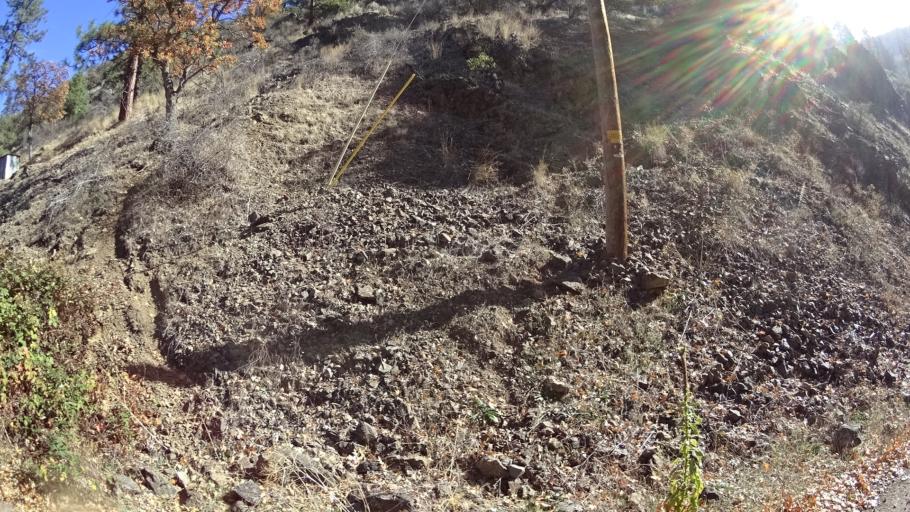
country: US
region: California
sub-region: Siskiyou County
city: Yreka
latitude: 41.8303
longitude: -122.6395
